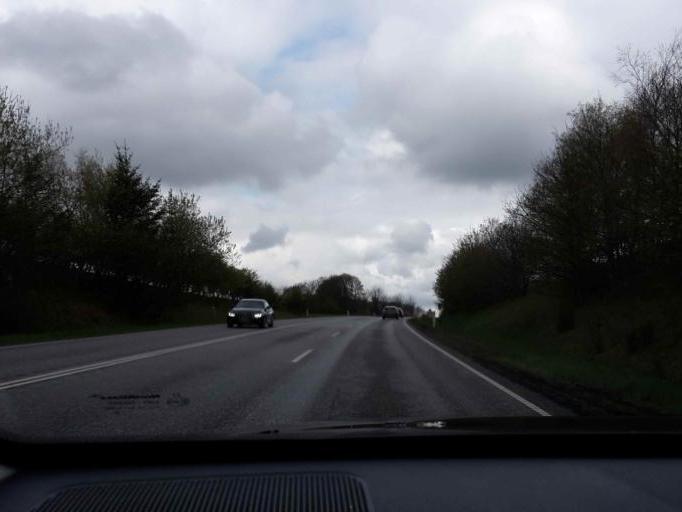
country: DK
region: South Denmark
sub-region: Vejle Kommune
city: Jelling
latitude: 55.6949
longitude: 9.3885
